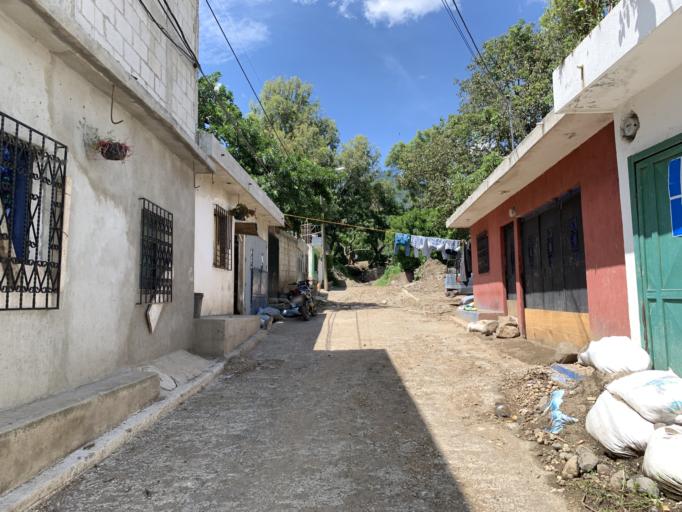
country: GT
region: Guatemala
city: Amatitlan
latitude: 14.4903
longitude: -90.6436
